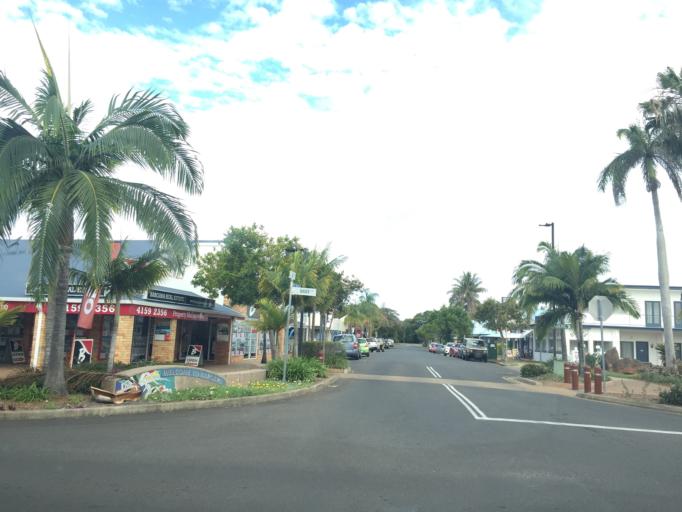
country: AU
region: Queensland
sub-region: Bundaberg
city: Bundaberg
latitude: -24.8149
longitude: 152.4629
